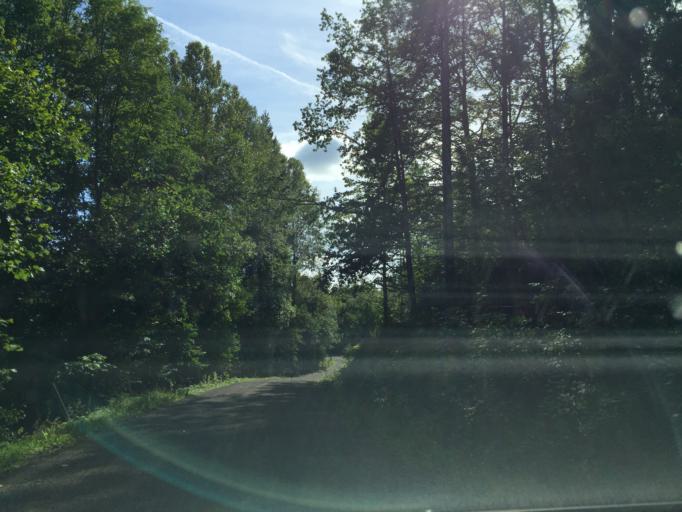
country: NO
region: Vestfold
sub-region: Hof
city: Hof
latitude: 59.4508
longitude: 10.1527
